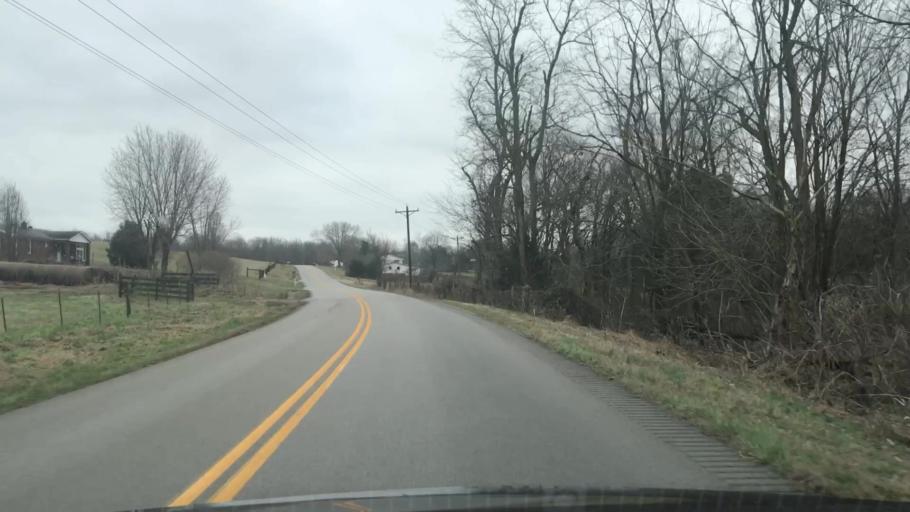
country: US
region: Kentucky
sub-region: Barren County
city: Glasgow
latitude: 36.9135
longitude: -85.8020
